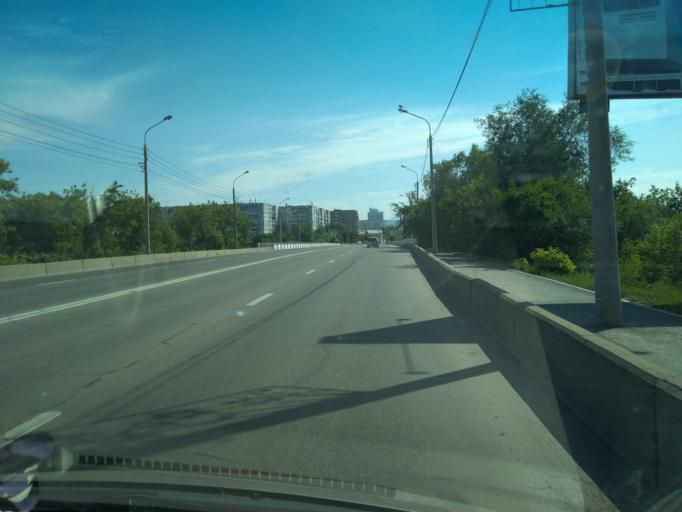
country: RU
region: Krasnoyarskiy
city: Krasnoyarsk
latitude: 56.0189
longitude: 92.8692
